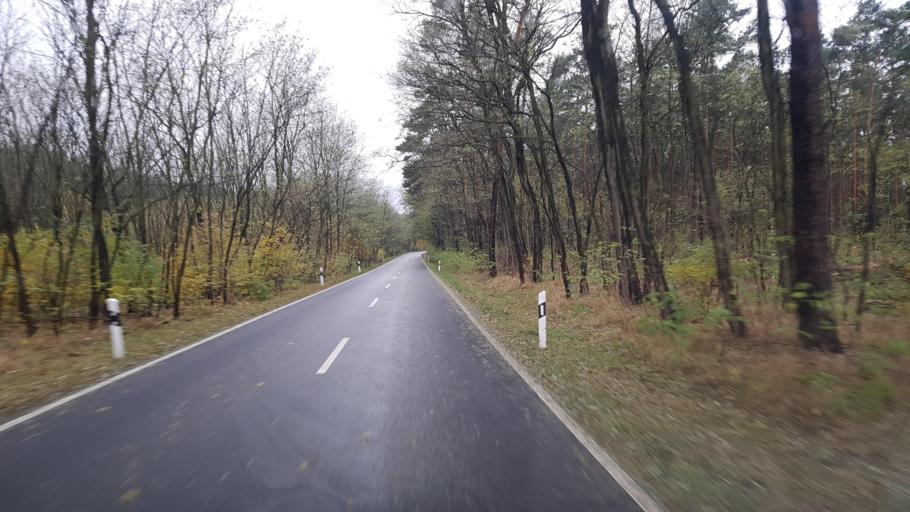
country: DE
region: Brandenburg
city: Drebkau
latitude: 51.6646
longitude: 14.2751
